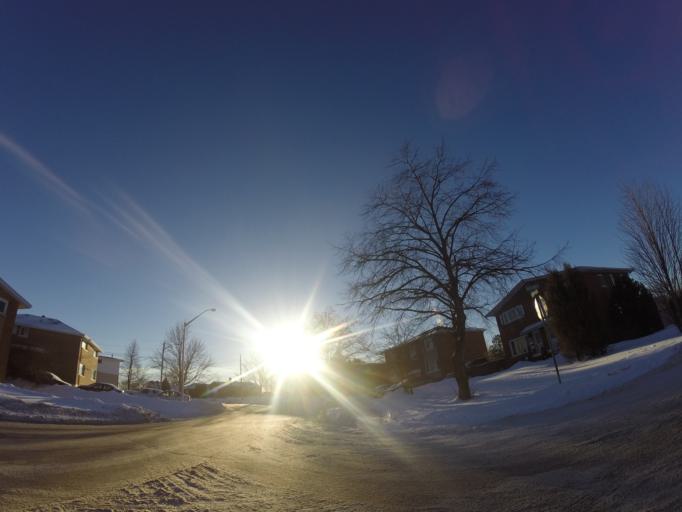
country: CA
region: Ontario
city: Greater Sudbury
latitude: 46.5055
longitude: -81.0027
